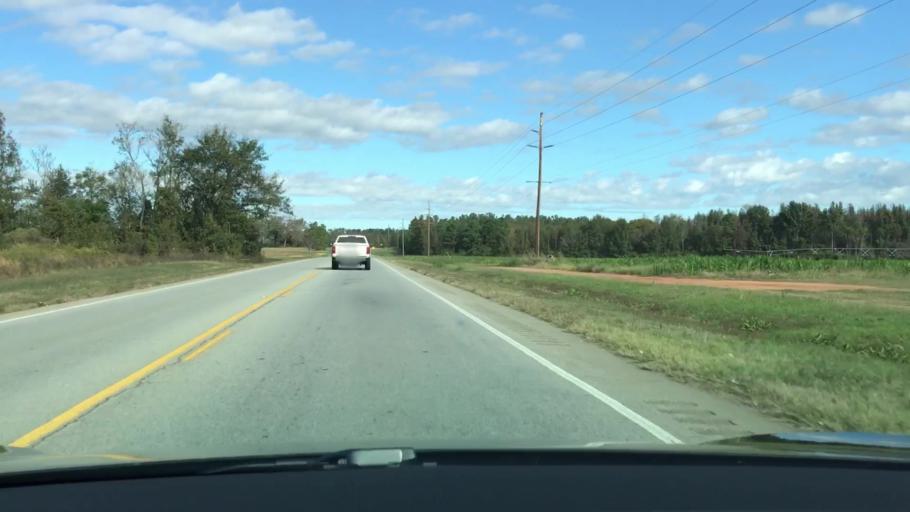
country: US
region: Georgia
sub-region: Jefferson County
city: Louisville
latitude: 33.0462
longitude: -82.4061
